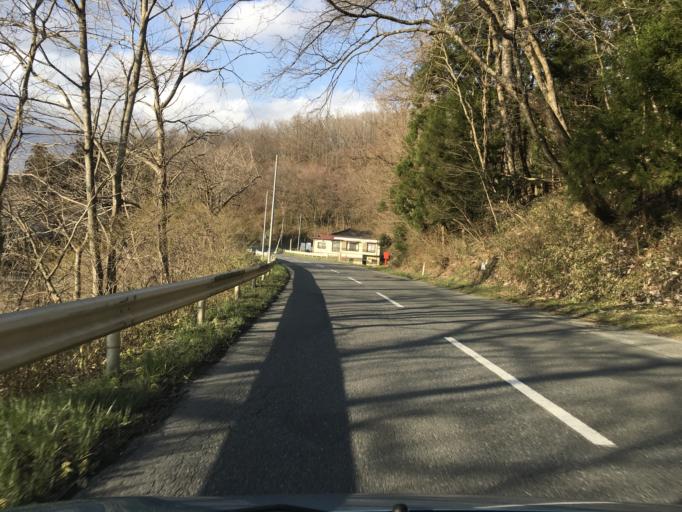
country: JP
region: Iwate
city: Ichinoseki
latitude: 38.8422
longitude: 141.3416
